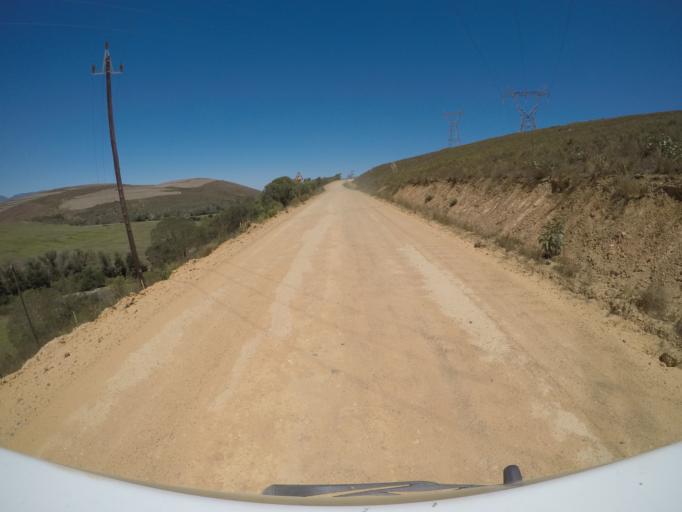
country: ZA
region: Western Cape
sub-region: Overberg District Municipality
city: Caledon
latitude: -34.2030
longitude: 19.2186
